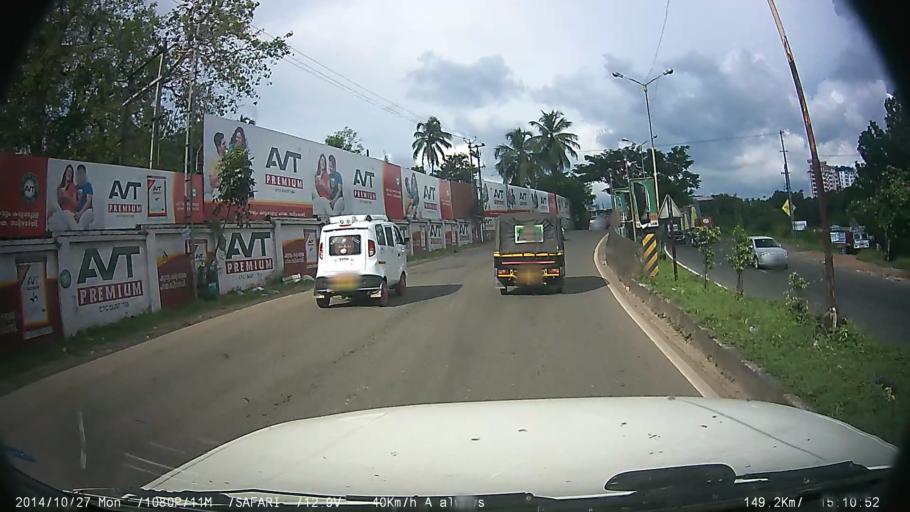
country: IN
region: Kerala
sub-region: Ernakulam
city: Aluva
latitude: 10.1248
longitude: 76.3402
